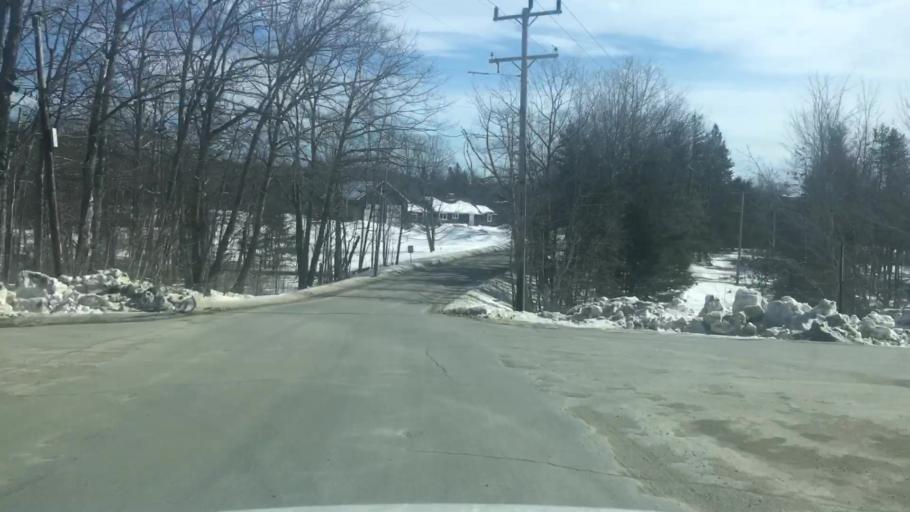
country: US
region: Maine
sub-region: Penobscot County
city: Holden
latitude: 44.7592
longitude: -68.6408
